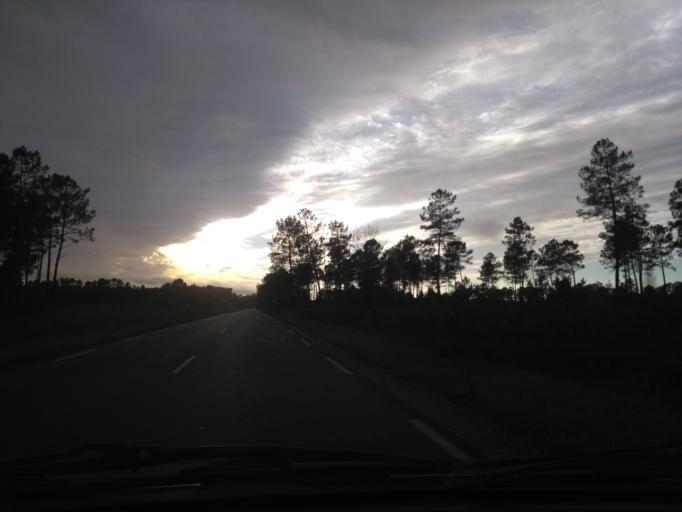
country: FR
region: Aquitaine
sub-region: Departement de la Gironde
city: Le Barp
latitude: 44.5976
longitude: -0.7112
